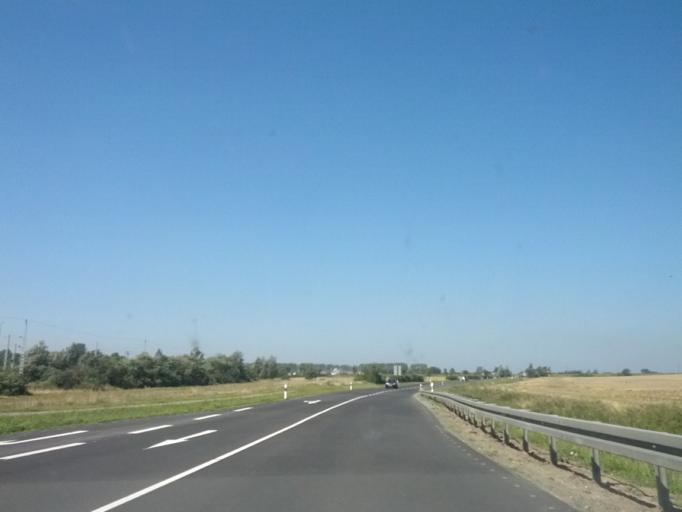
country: DE
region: Mecklenburg-Vorpommern
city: Sagard
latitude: 54.5053
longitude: 13.5479
